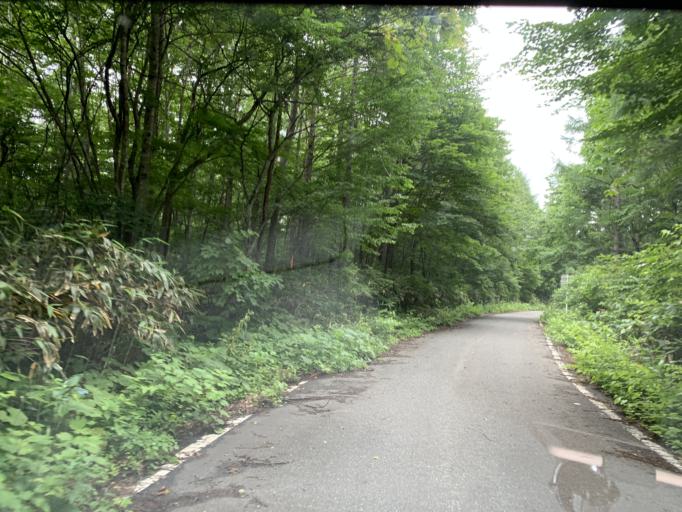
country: JP
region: Iwate
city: Ichinoseki
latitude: 38.9415
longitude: 140.8729
